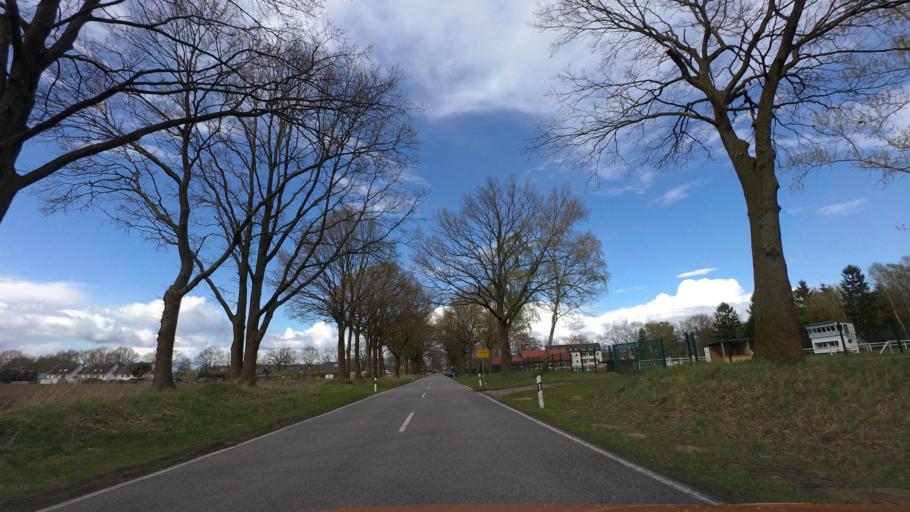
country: DE
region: Mecklenburg-Vorpommern
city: Nostorf
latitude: 53.4270
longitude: 10.6840
